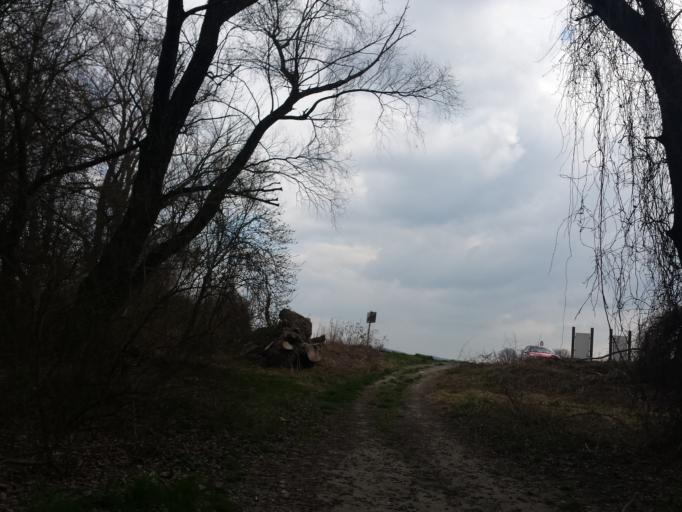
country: AT
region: Lower Austria
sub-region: Politischer Bezirk Bruck an der Leitha
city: Hainburg an der Donau
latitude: 48.1684
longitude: 16.9784
